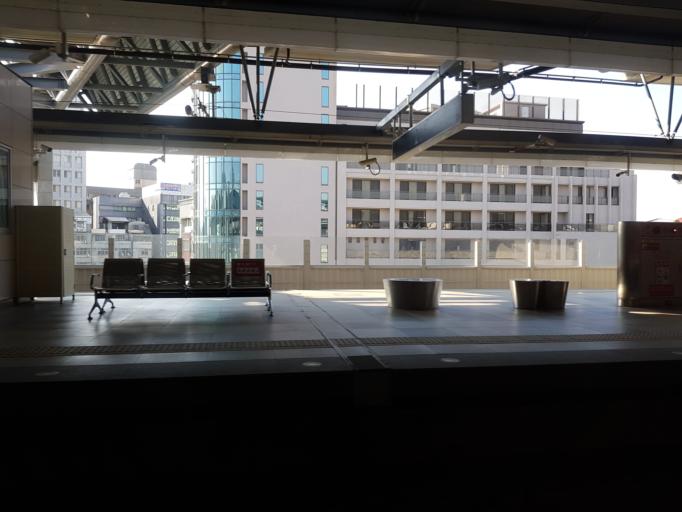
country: TW
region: Taiwan
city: Fengyuan
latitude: 24.2547
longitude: 120.7238
